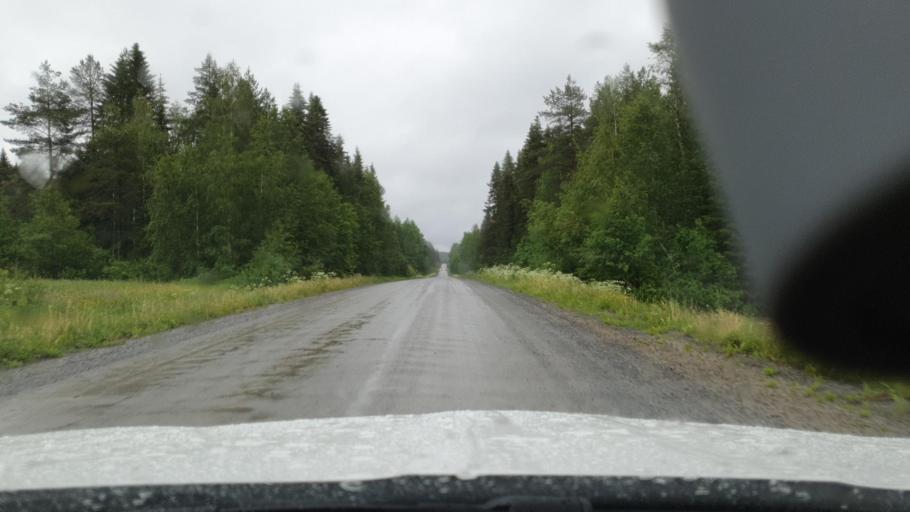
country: SE
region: Vaesterbotten
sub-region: Skelleftea Kommun
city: Burtraesk
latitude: 64.3834
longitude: 20.3185
